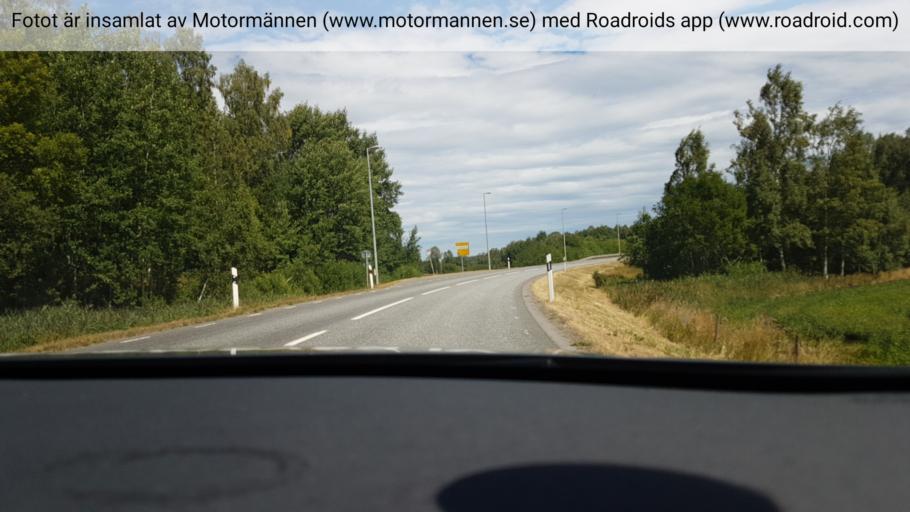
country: SE
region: Joenkoeping
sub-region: Tranas Kommun
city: Tranas
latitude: 57.9876
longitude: 14.8419
